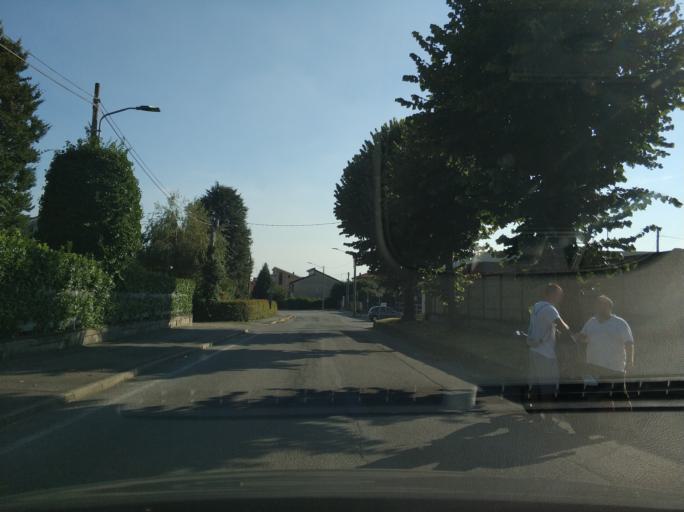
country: IT
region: Piedmont
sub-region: Provincia di Torino
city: San Maurizio
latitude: 45.2136
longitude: 7.6309
